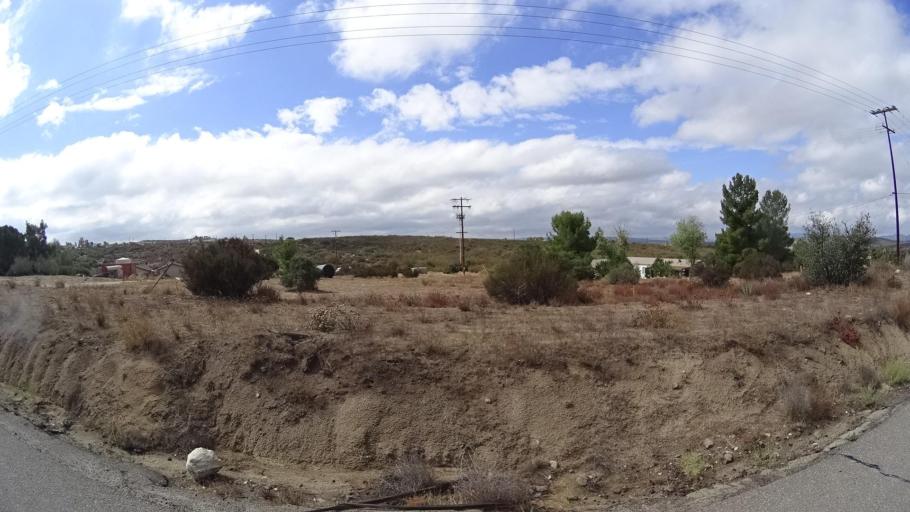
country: US
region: California
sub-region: San Diego County
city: Campo
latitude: 32.6714
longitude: -116.3187
